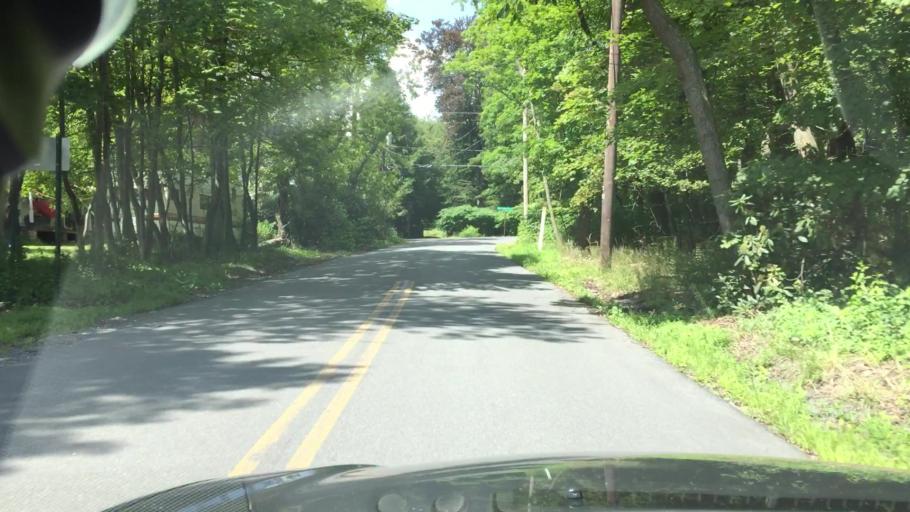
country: US
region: Pennsylvania
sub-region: Luzerne County
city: Freeland
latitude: 41.0308
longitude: -75.9161
